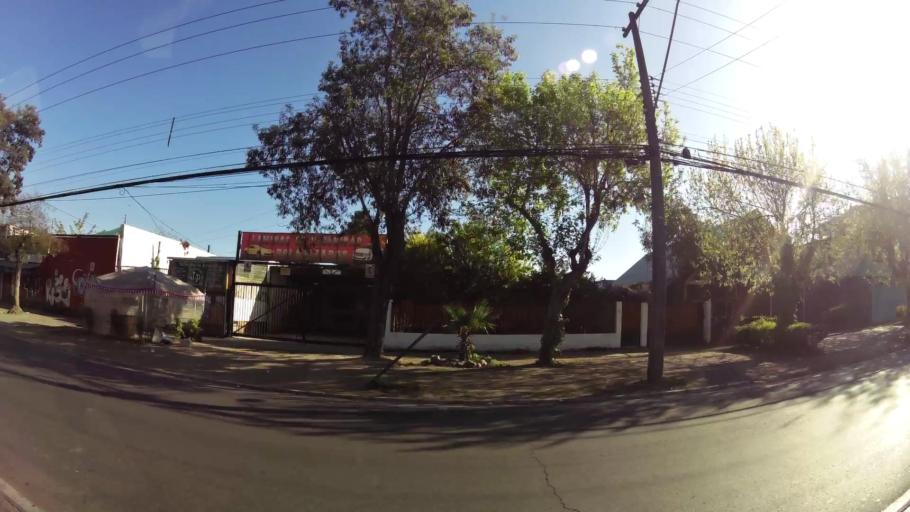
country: CL
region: Santiago Metropolitan
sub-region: Provincia de Santiago
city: Villa Presidente Frei, Nunoa, Santiago, Chile
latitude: -33.4626
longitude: -70.5587
